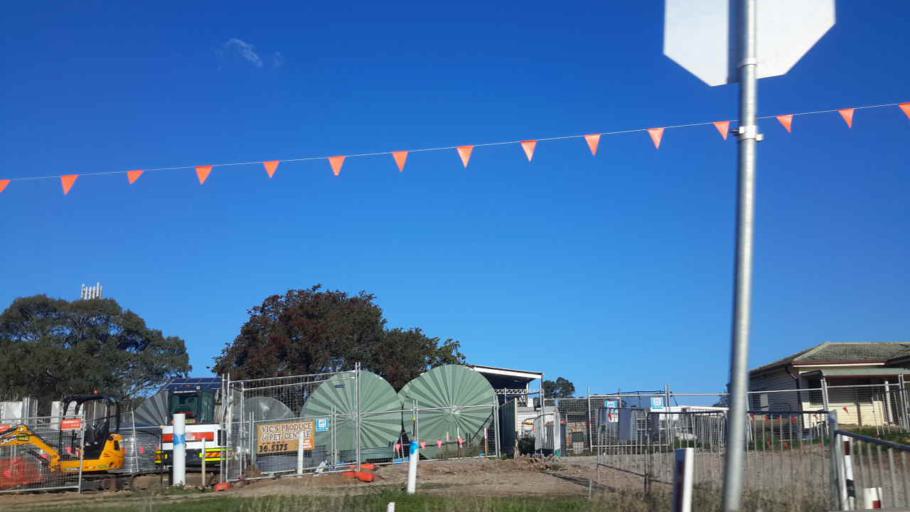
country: AU
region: New South Wales
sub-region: Penrith Municipality
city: Kingswood Park
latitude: -33.7912
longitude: 150.6998
